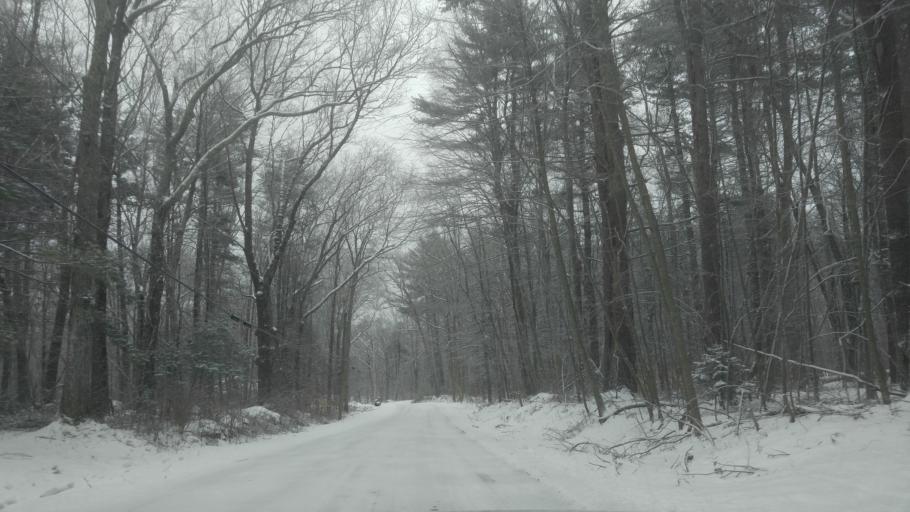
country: US
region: Rhode Island
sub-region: Providence County
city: Foster
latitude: 41.8257
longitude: -71.7366
